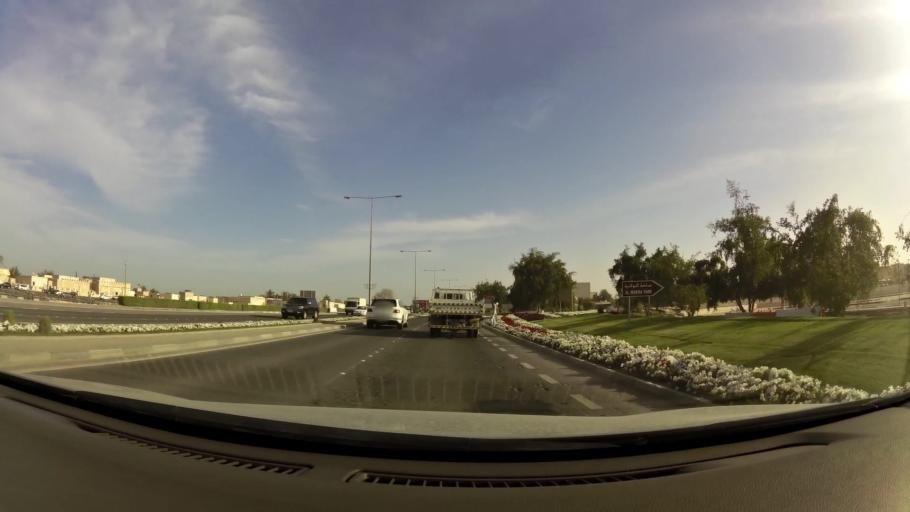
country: QA
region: Al Wakrah
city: Al Wakrah
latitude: 25.1720
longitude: 51.6070
